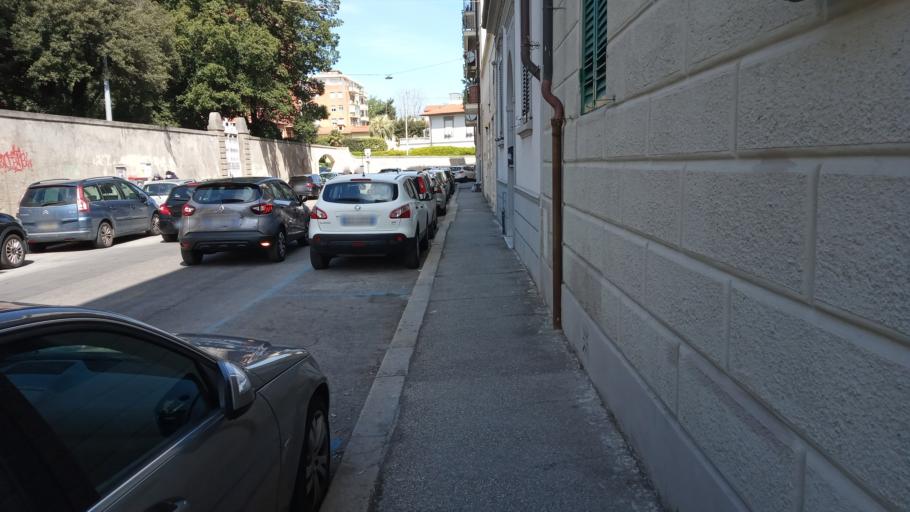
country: IT
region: Tuscany
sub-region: Provincia di Livorno
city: Livorno
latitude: 43.5390
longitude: 10.3128
